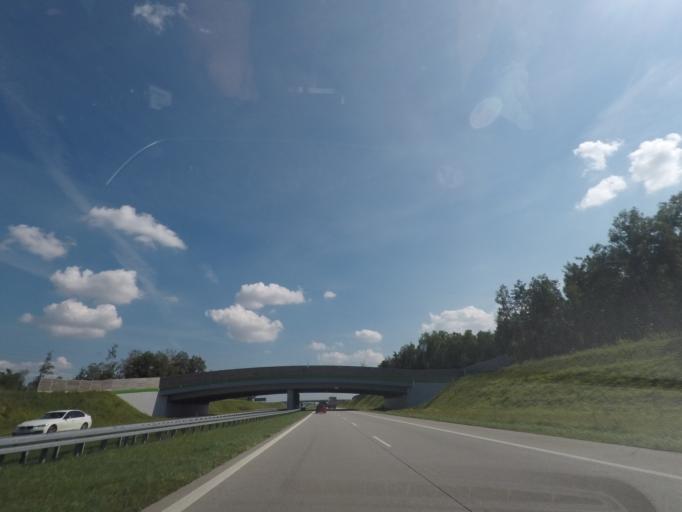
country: PL
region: Lodz Voivodeship
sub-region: Powiat lodzki wschodni
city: Tuszyn
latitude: 51.6057
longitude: 19.5759
